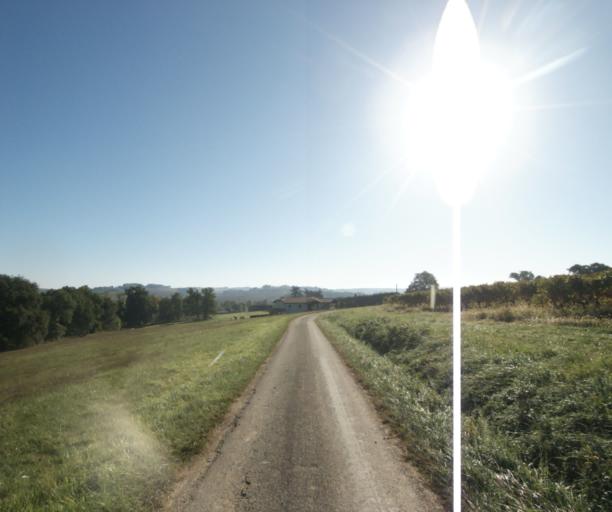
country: FR
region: Midi-Pyrenees
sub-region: Departement du Gers
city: Gondrin
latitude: 43.8371
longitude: 0.2790
